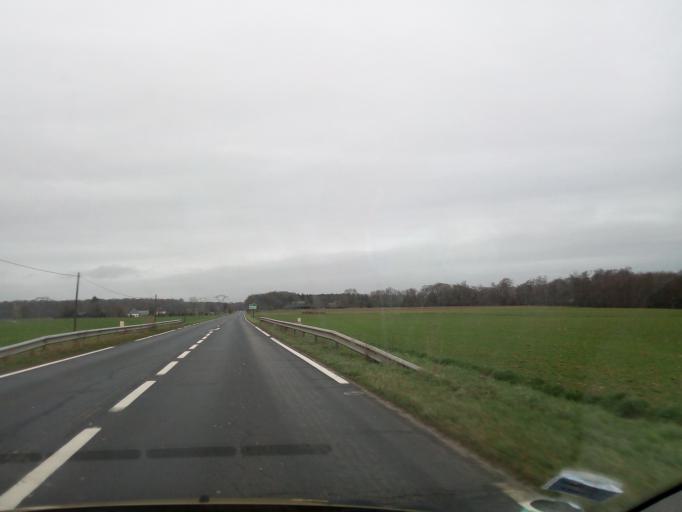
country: FR
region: Haute-Normandie
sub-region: Departement de l'Eure
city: Hauville
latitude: 49.4052
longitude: 0.7972
